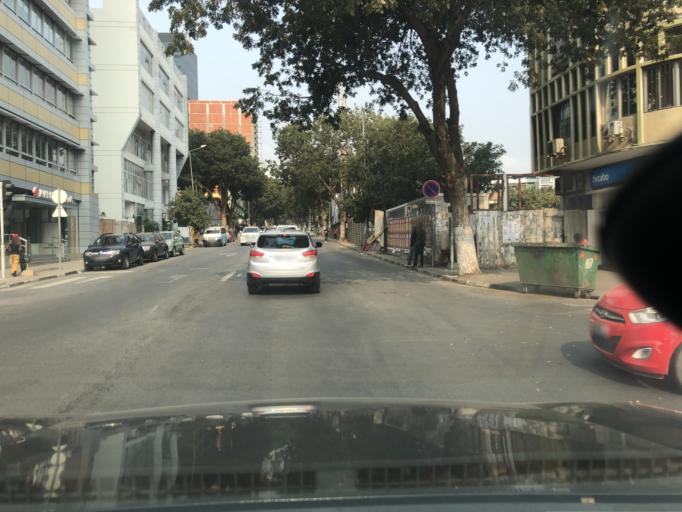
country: AO
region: Luanda
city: Luanda
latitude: -8.8182
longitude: 13.2409
